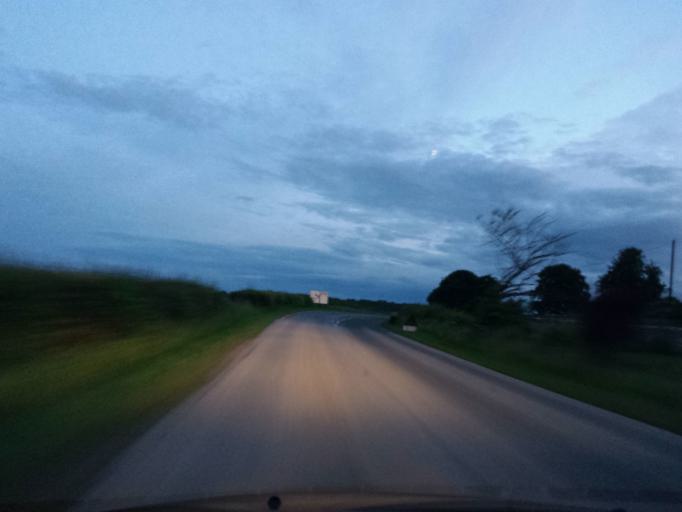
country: GB
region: Scotland
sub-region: The Scottish Borders
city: Duns
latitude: 55.7546
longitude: -2.4025
